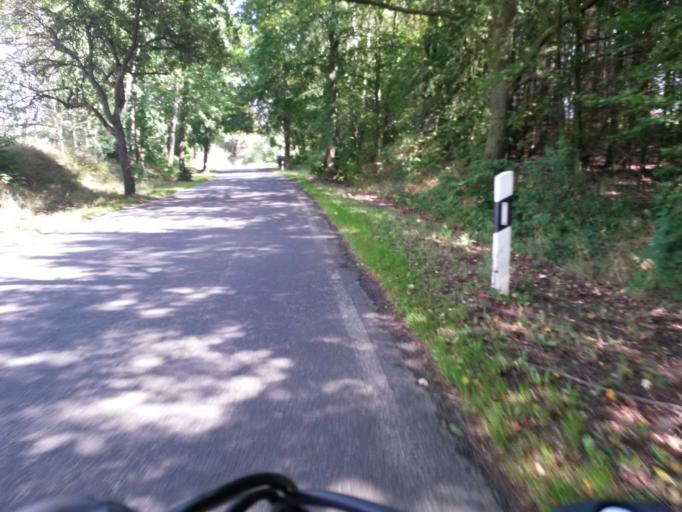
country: DE
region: Brandenburg
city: Angermunde
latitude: 53.0070
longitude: 13.9137
